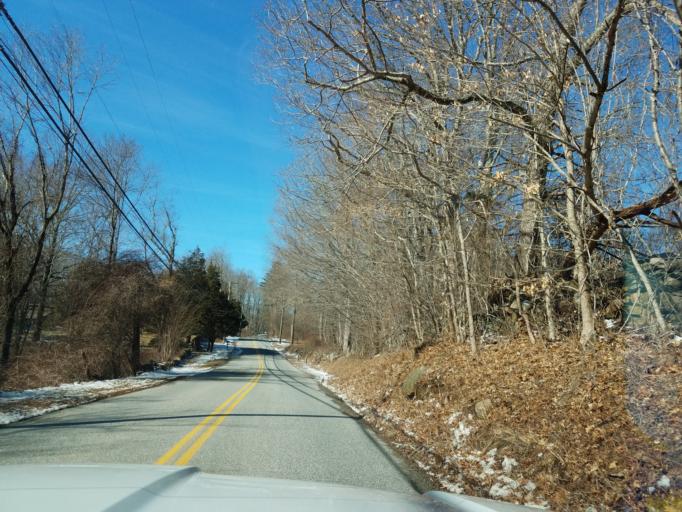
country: US
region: Connecticut
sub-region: New London County
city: Old Mystic
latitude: 41.4454
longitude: -71.9086
